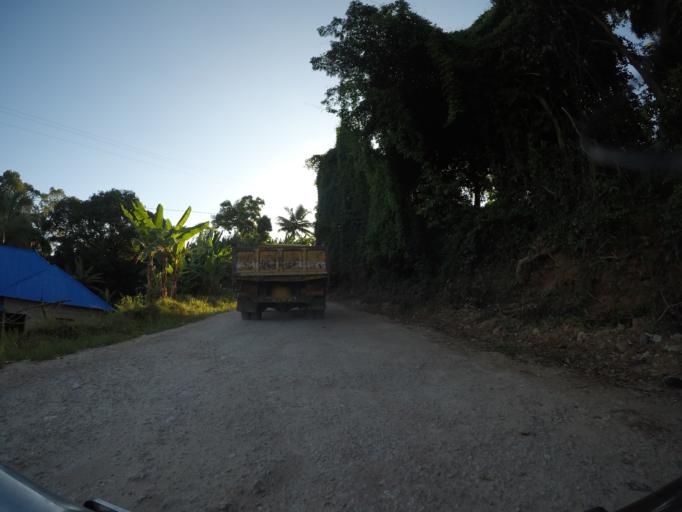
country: TZ
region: Pemba South
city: Uwelini
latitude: -5.3757
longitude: 39.6697
